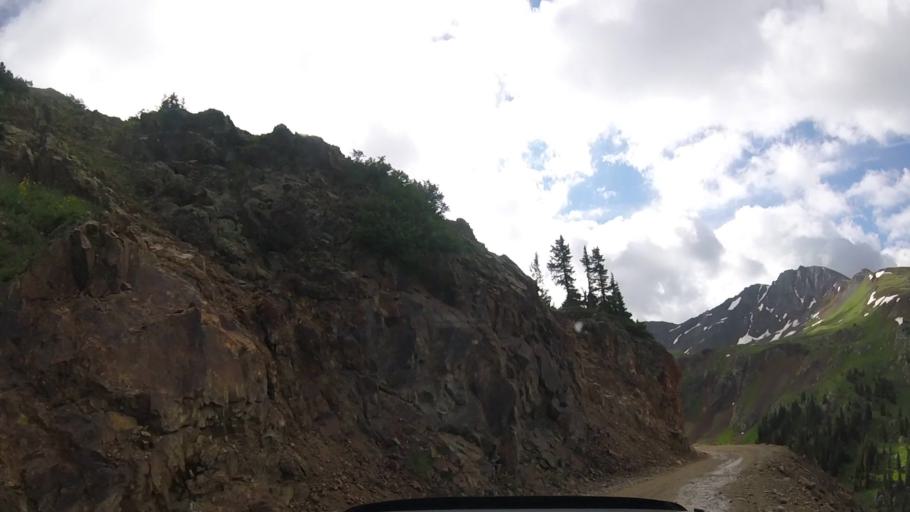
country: US
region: Colorado
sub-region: San Juan County
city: Silverton
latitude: 37.9136
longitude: -107.6372
